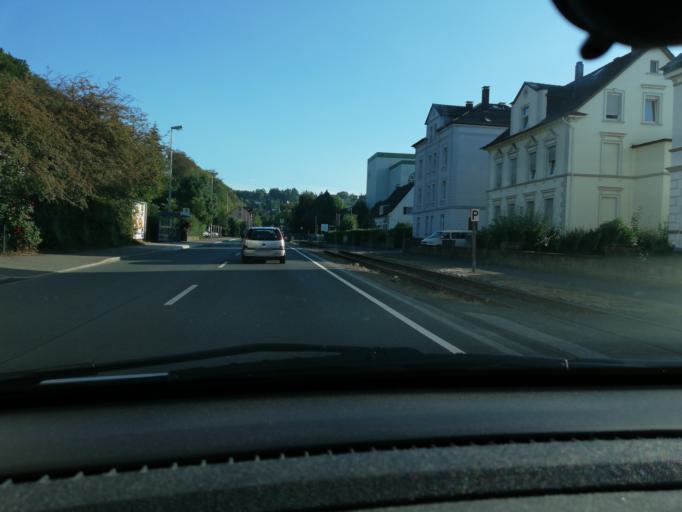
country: DE
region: North Rhine-Westphalia
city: Gevelsberg
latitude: 51.3160
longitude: 7.3417
